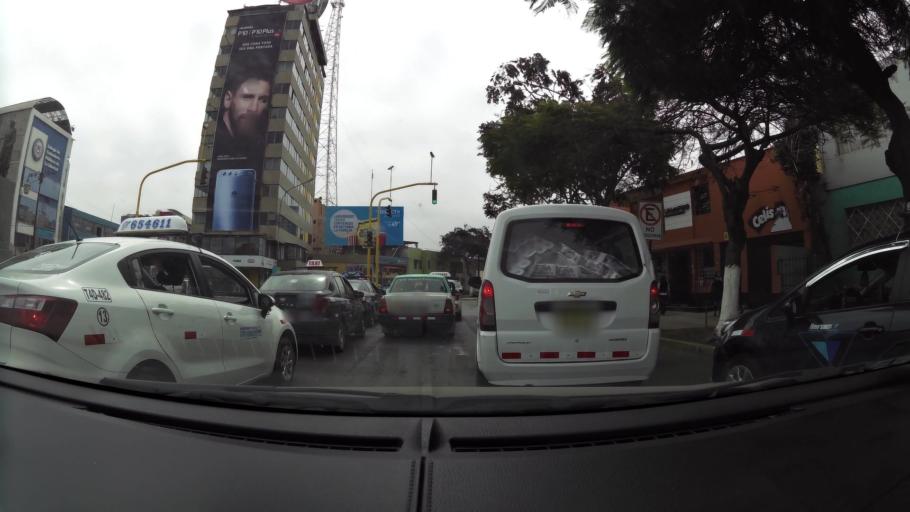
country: PE
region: La Libertad
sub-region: Provincia de Trujillo
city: Trujillo
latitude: -8.1140
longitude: -79.0325
